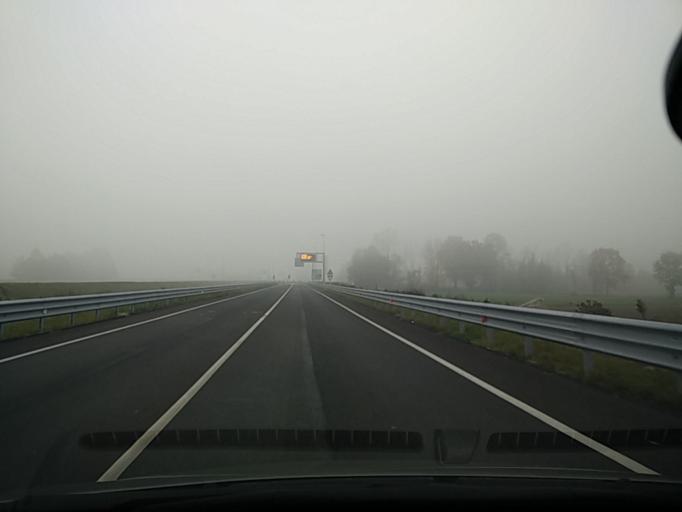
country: IT
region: Veneto
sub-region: Provincia di Venezia
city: Martellago
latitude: 45.5562
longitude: 12.1598
